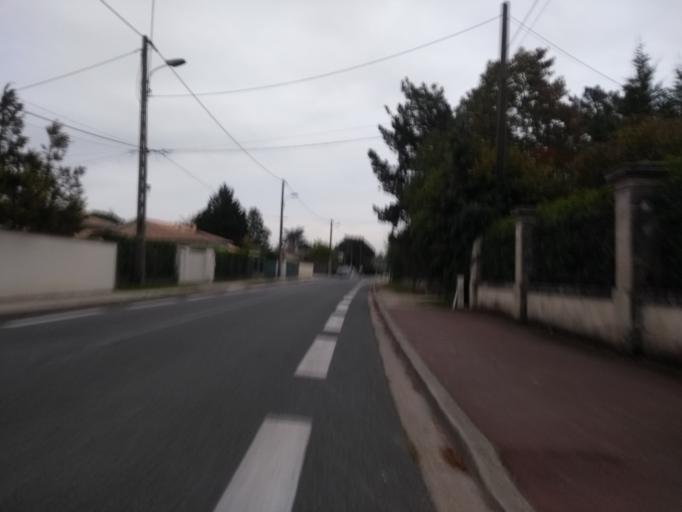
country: FR
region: Aquitaine
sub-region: Departement de la Gironde
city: Gradignan
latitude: 44.7751
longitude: -0.6003
